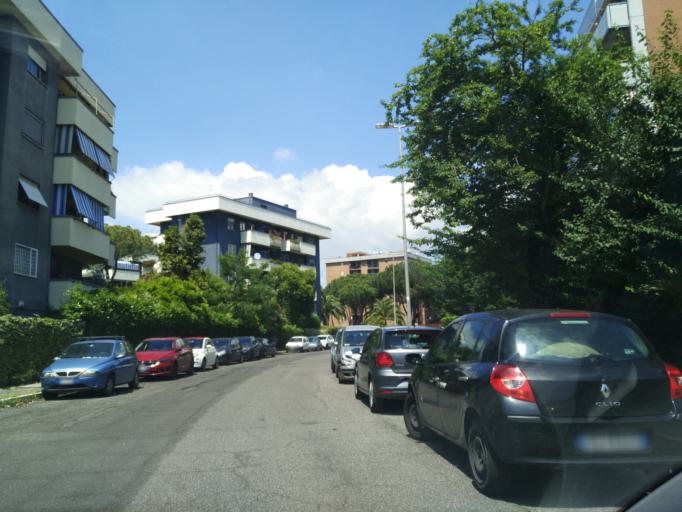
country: IT
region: Latium
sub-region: Citta metropolitana di Roma Capitale
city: Vitinia
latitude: 41.8085
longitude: 12.4349
